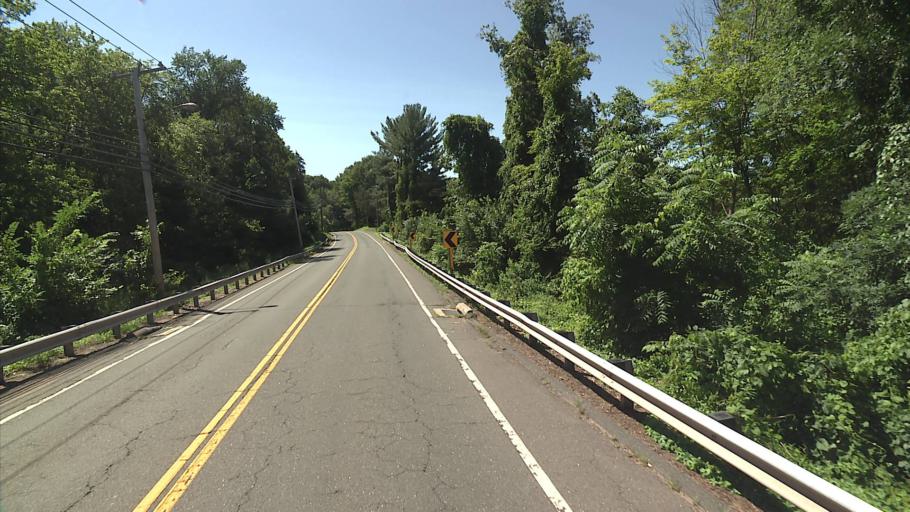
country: US
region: Connecticut
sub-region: Hartford County
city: Farmington
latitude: 41.7607
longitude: -72.8193
